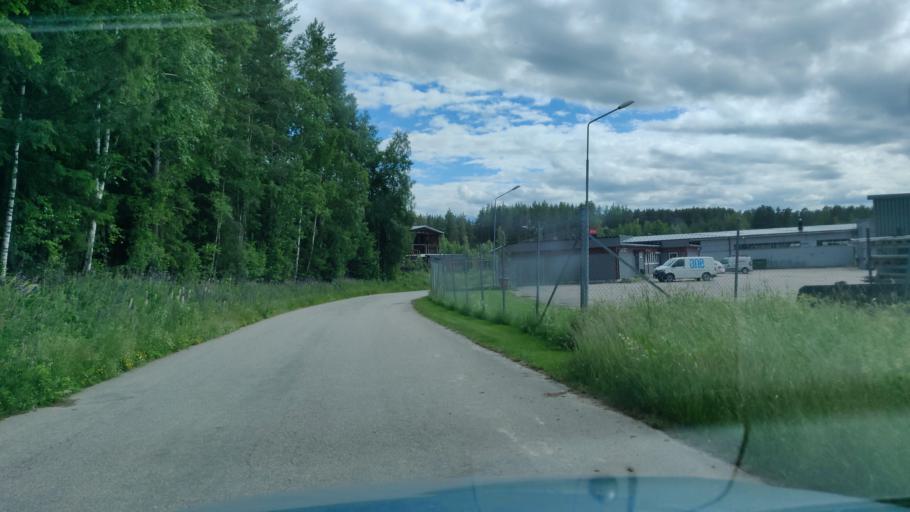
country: SE
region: Vaermland
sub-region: Hagfors Kommun
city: Hagfors
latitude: 60.0452
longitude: 13.7126
